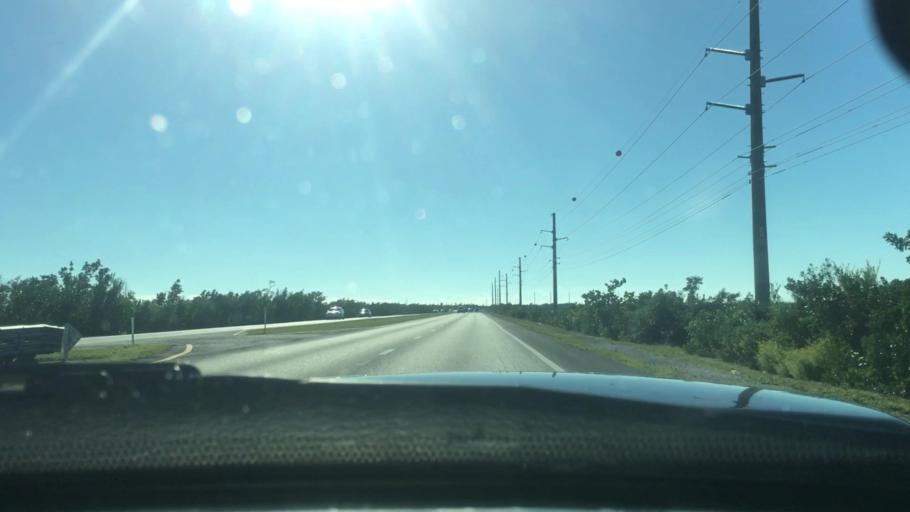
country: US
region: Florida
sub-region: Monroe County
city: Big Coppitt Key
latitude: 24.5851
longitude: -81.6991
